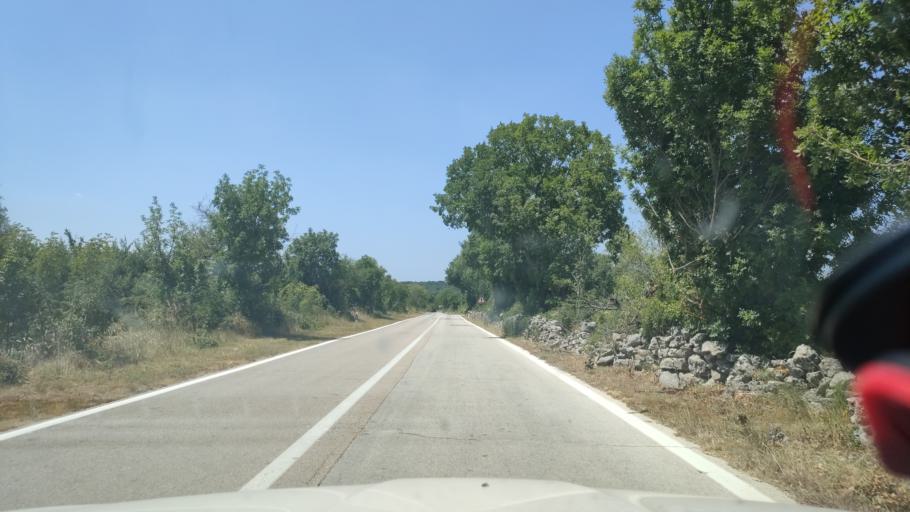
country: HR
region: Sibensko-Kniniska
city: Kistanje
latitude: 44.0161
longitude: 16.0134
